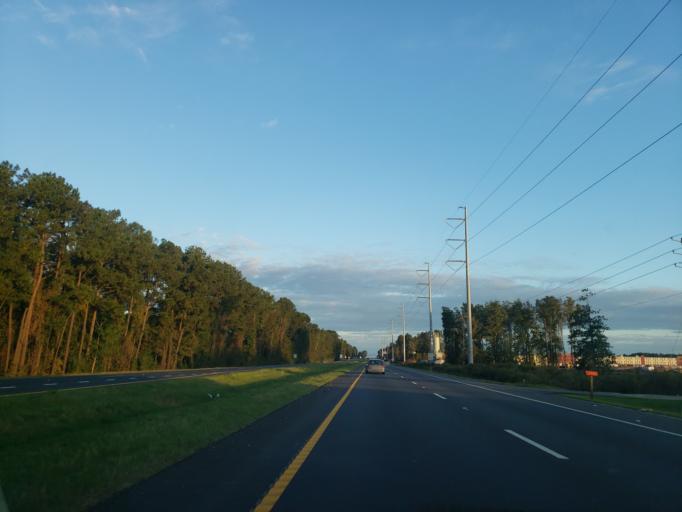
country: US
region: Georgia
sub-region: Chatham County
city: Port Wentworth
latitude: 32.1377
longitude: -81.1743
